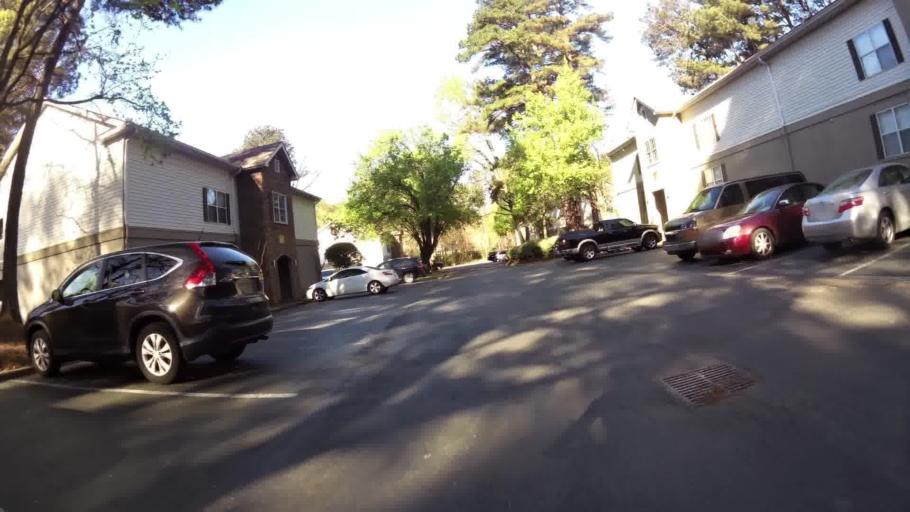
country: US
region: Georgia
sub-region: DeKalb County
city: Clarkston
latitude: 33.8390
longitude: -84.2616
